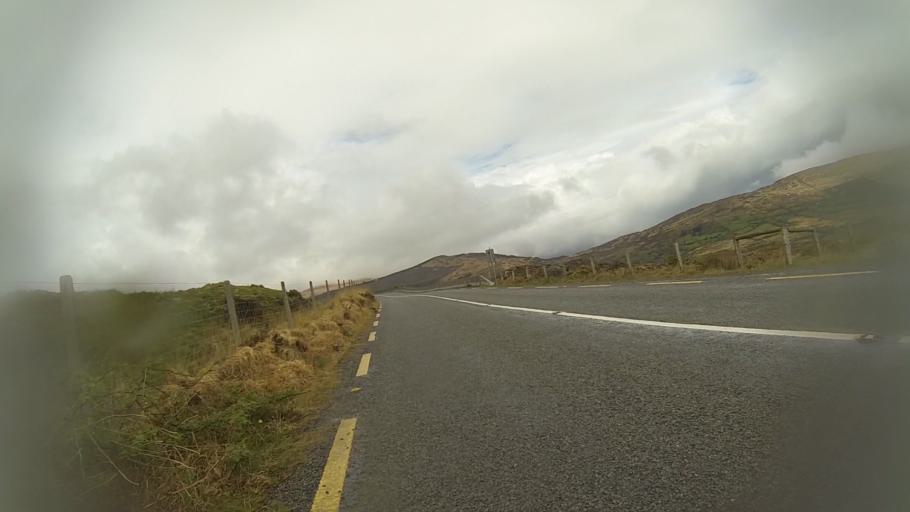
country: IE
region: Munster
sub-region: Ciarrai
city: Kenmare
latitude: 51.8015
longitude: -9.5743
